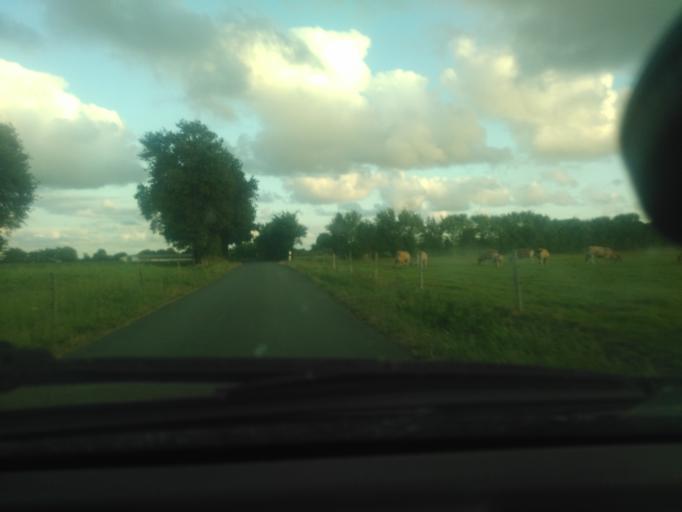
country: FR
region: Pays de la Loire
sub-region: Departement de la Vendee
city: La Ferriere
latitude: 46.7073
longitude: -1.2999
